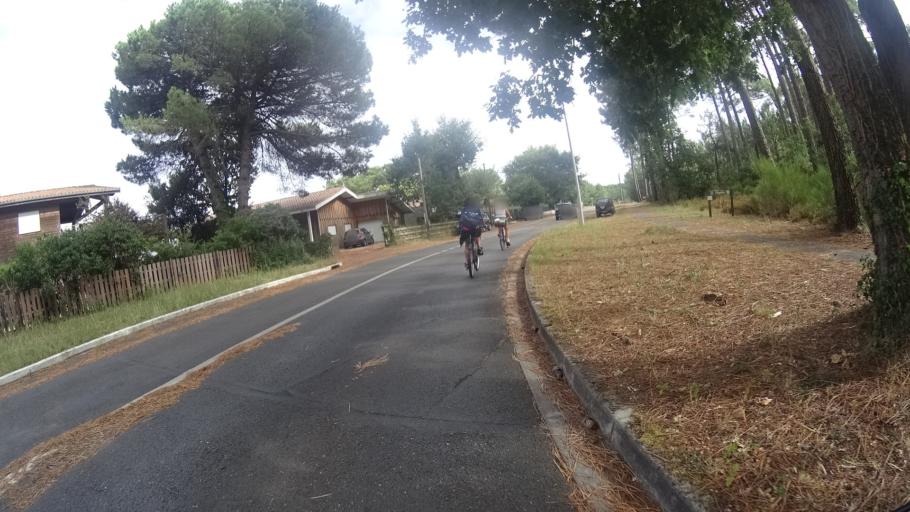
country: FR
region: Aquitaine
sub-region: Departement de la Gironde
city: Lacanau
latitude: 44.9925
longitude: -1.1464
